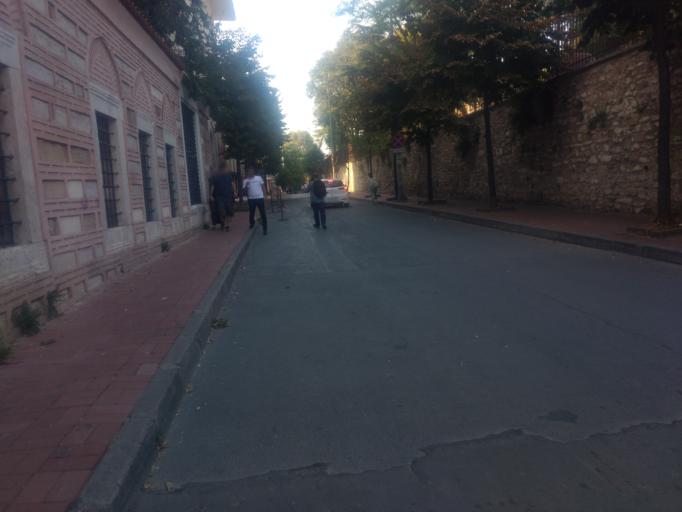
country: TR
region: Istanbul
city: Eminoenue
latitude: 41.0127
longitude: 28.9625
